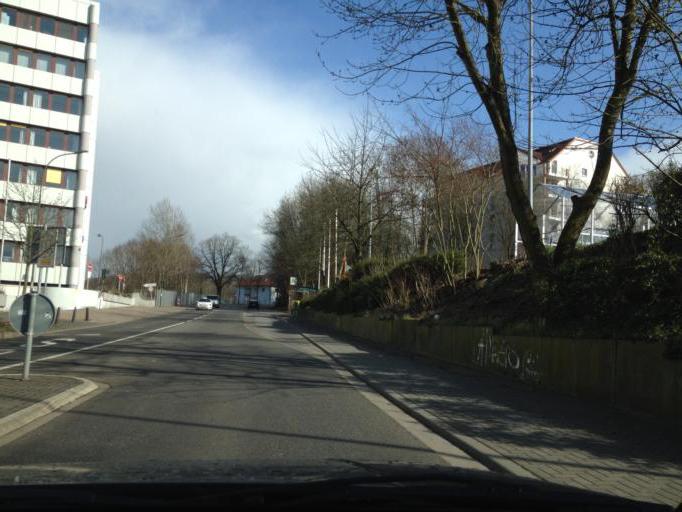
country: DE
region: Saarland
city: Neunkirchen
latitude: 49.3504
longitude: 7.1840
